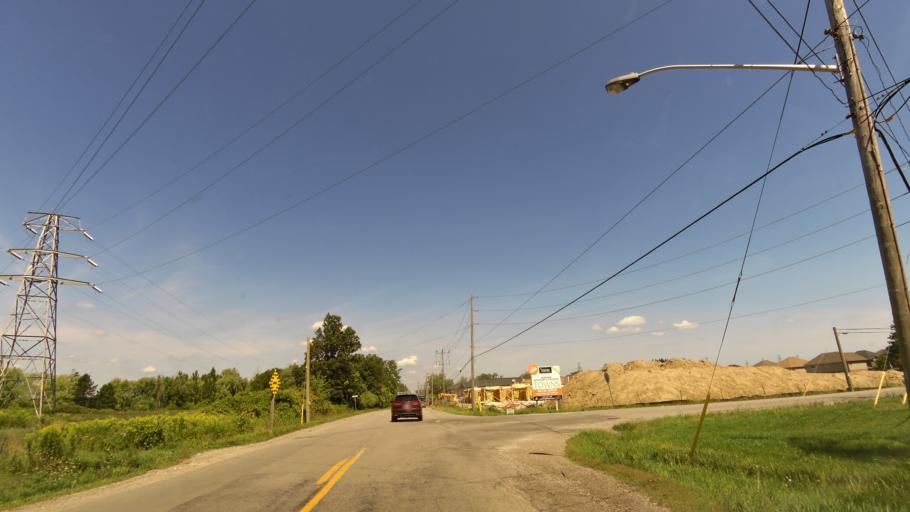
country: CA
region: Ontario
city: Ancaster
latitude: 43.1988
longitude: -79.9326
